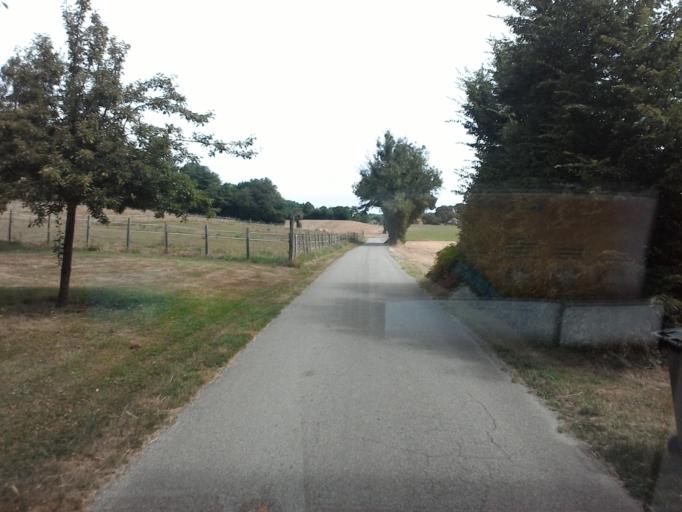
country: FR
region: Rhone-Alpes
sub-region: Departement de l'Isere
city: Montferrat
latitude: 45.4978
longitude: 5.5681
